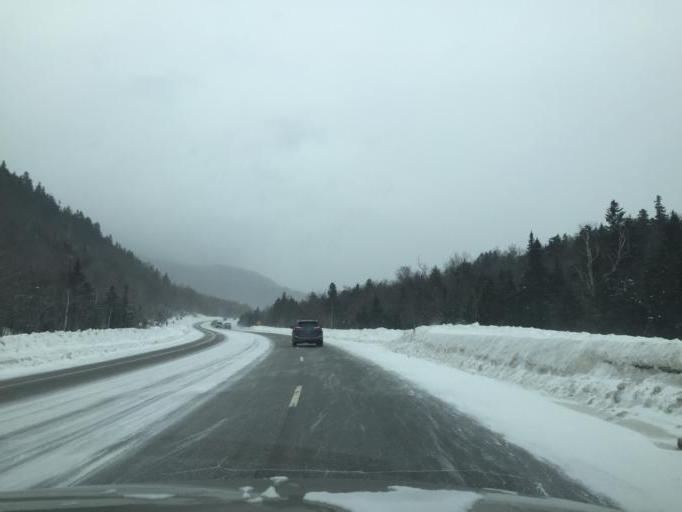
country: US
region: New Hampshire
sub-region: Coos County
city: Gorham
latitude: 44.2463
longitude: -71.2531
